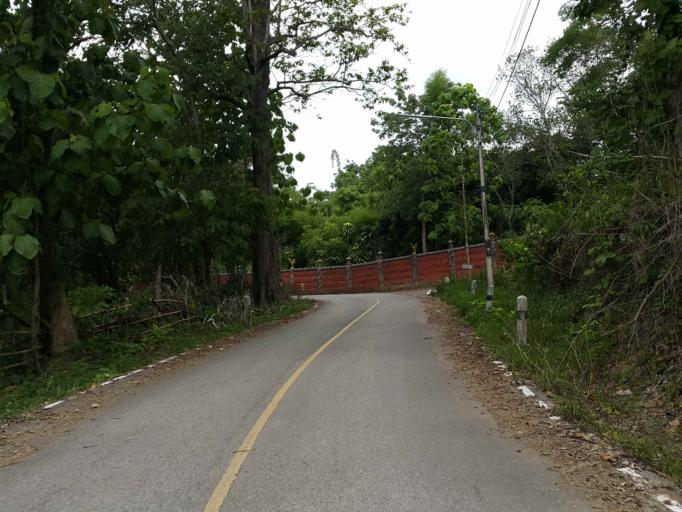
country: TH
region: Chiang Mai
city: Hang Dong
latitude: 18.7587
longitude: 98.9050
